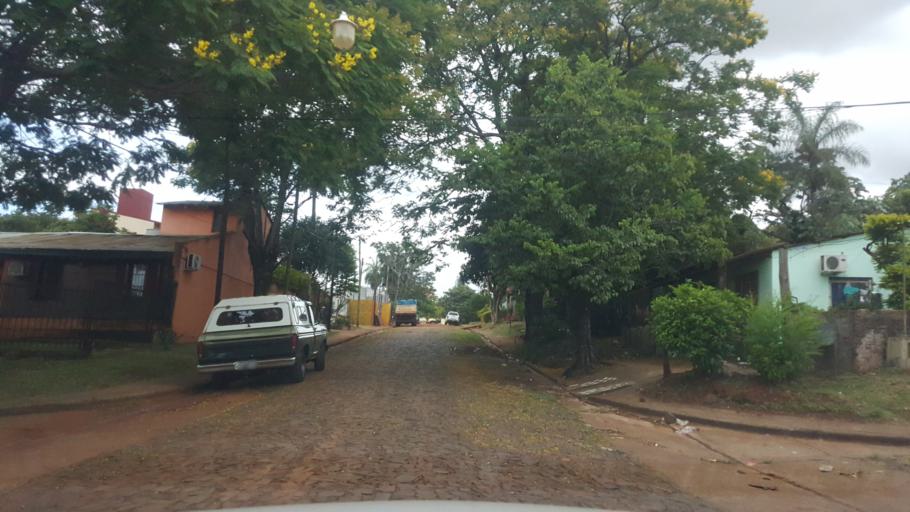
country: AR
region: Misiones
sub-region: Departamento de Capital
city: Posadas
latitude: -27.3962
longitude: -55.8962
